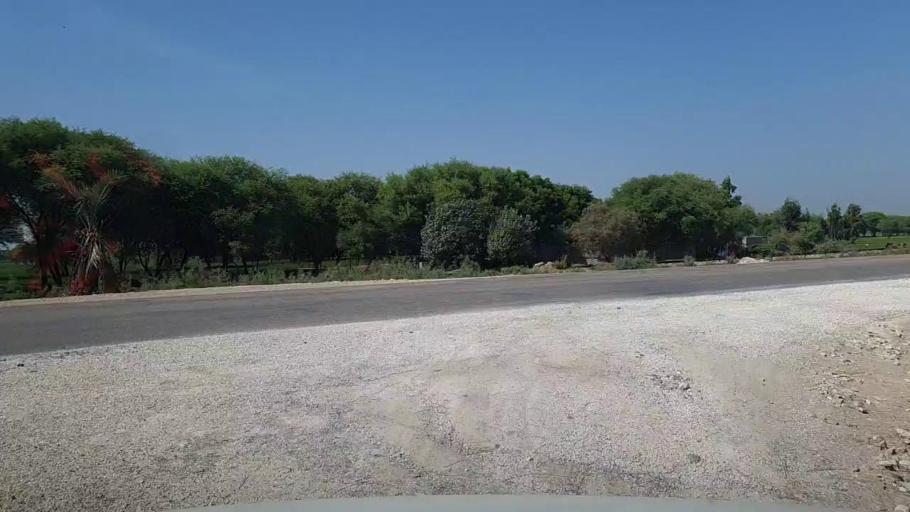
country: PK
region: Sindh
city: Kandhkot
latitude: 28.3404
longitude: 69.3623
